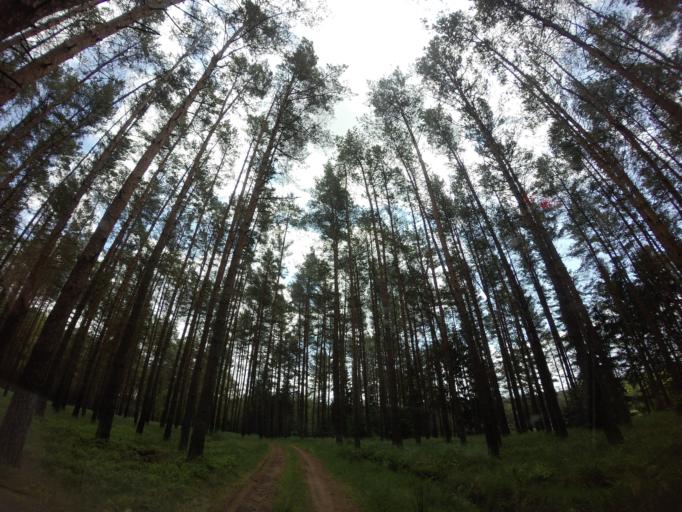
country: PL
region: West Pomeranian Voivodeship
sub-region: Powiat drawski
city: Kalisz Pomorski
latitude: 53.2191
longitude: 15.9480
